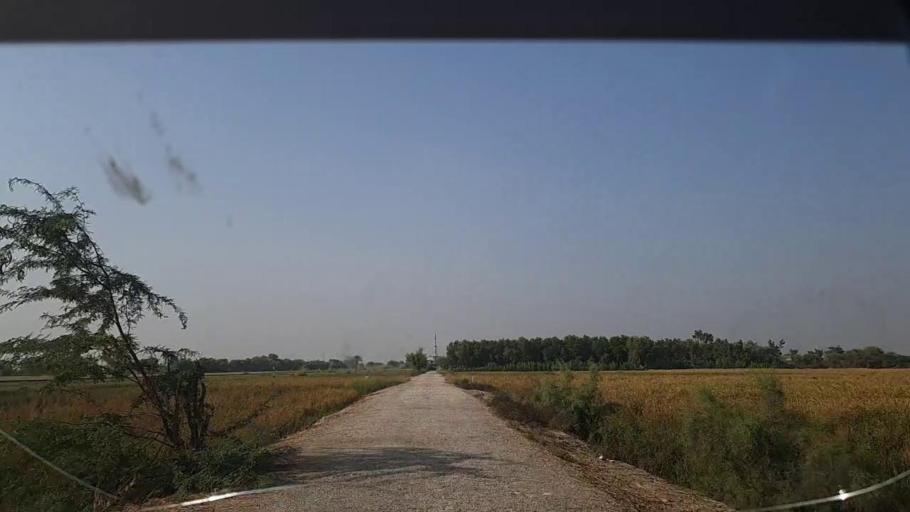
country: PK
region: Sindh
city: Shikarpur
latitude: 28.1185
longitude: 68.5726
